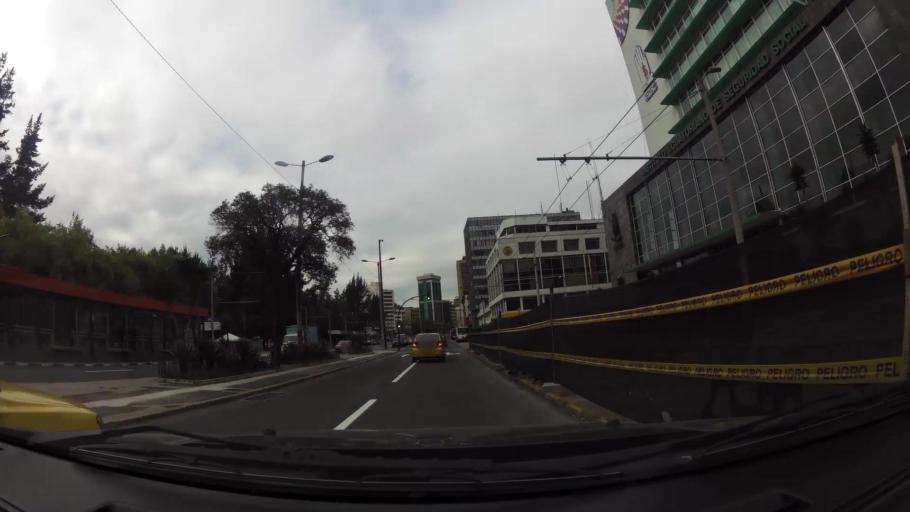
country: EC
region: Pichincha
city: Quito
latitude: -0.2086
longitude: -78.5002
